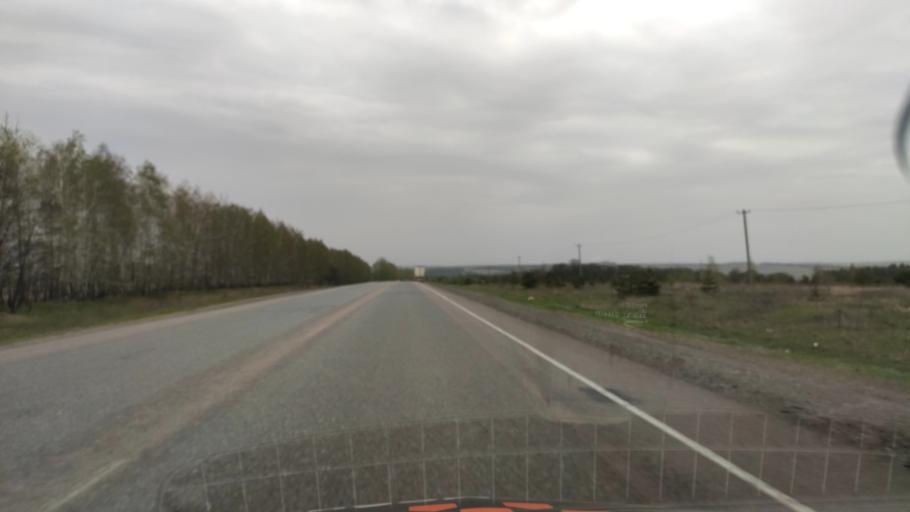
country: RU
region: Kursk
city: Gorshechnoye
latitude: 51.4569
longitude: 37.9209
